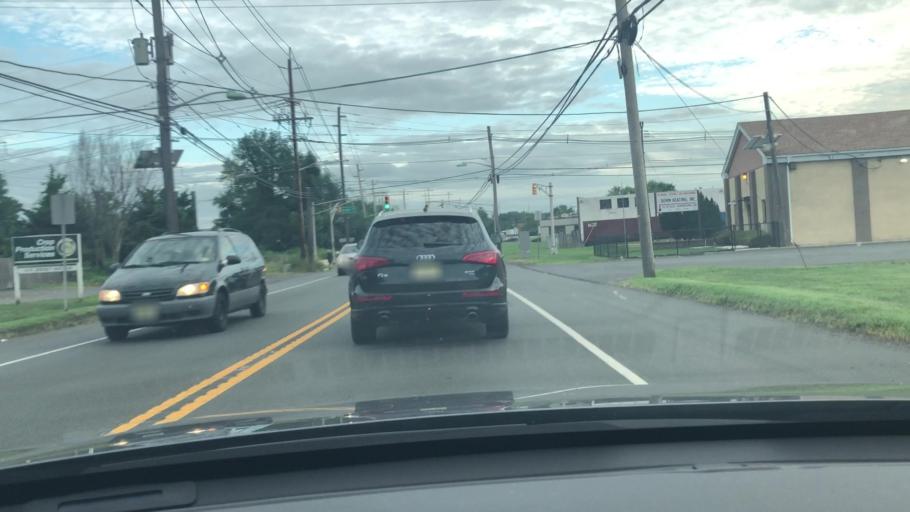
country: US
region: New Jersey
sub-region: Somerset County
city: Somerset
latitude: 40.4612
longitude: -74.4839
